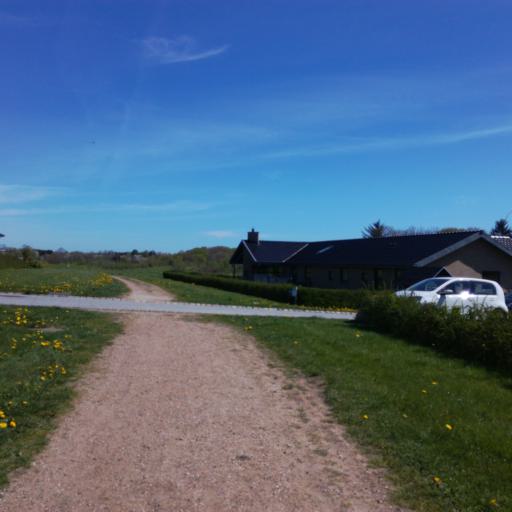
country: DK
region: South Denmark
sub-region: Vejle Kommune
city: Borkop
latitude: 55.6297
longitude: 9.6597
